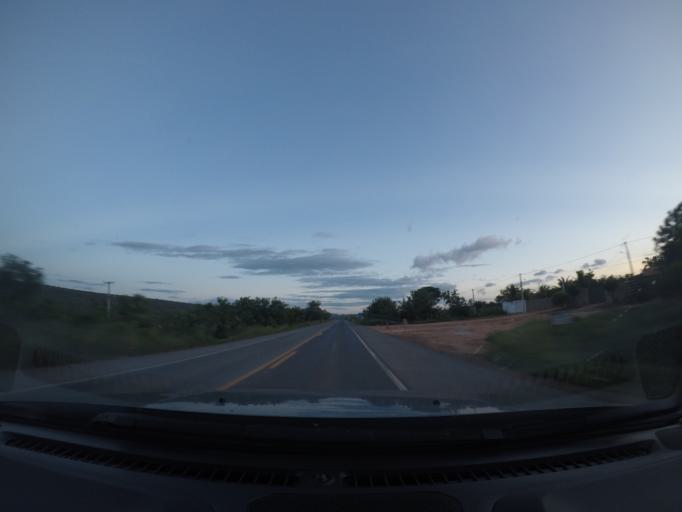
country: BR
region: Bahia
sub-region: Seabra
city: Seabra
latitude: -12.4616
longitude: -41.7474
